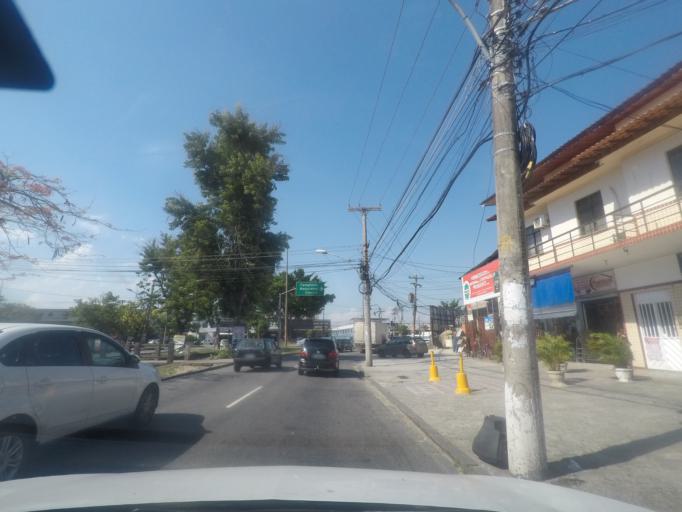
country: BR
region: Rio de Janeiro
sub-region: Sao Joao De Meriti
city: Sao Joao de Meriti
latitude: -22.8776
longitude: -43.3697
